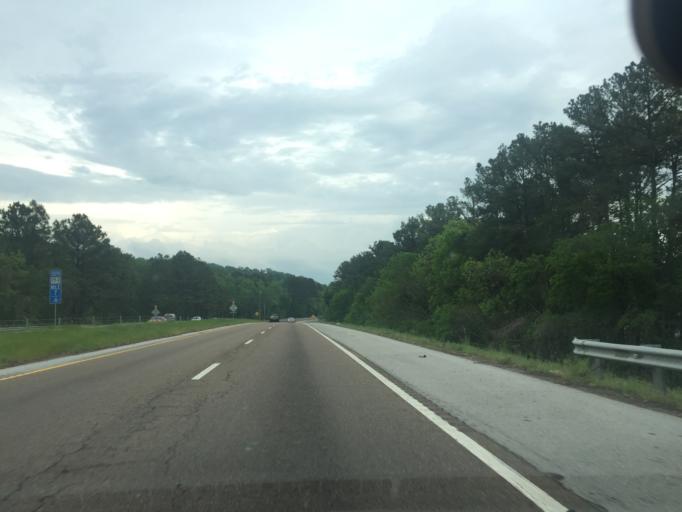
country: US
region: Tennessee
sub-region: Hamilton County
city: East Chattanooga
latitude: 35.1167
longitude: -85.2332
